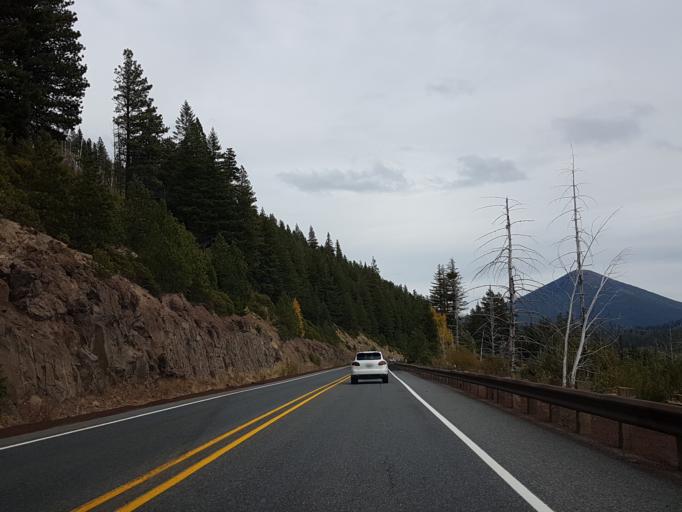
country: US
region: Oregon
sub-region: Deschutes County
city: Sisters
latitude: 44.4187
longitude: -121.7773
